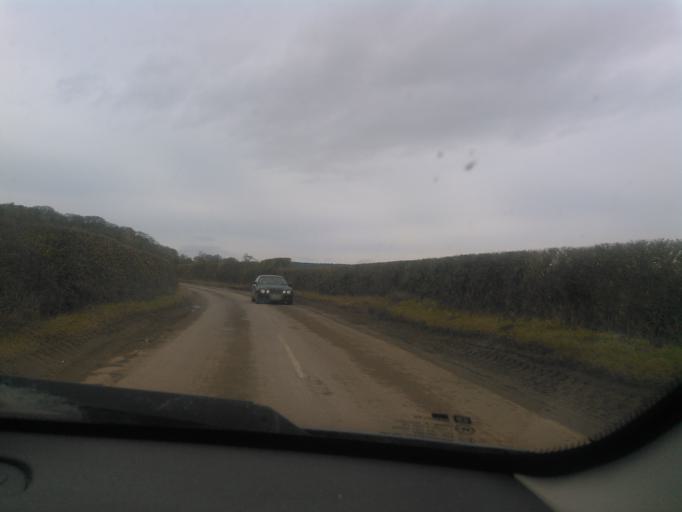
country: GB
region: England
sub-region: Shropshire
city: Shawbury
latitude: 52.8212
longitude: -2.6679
